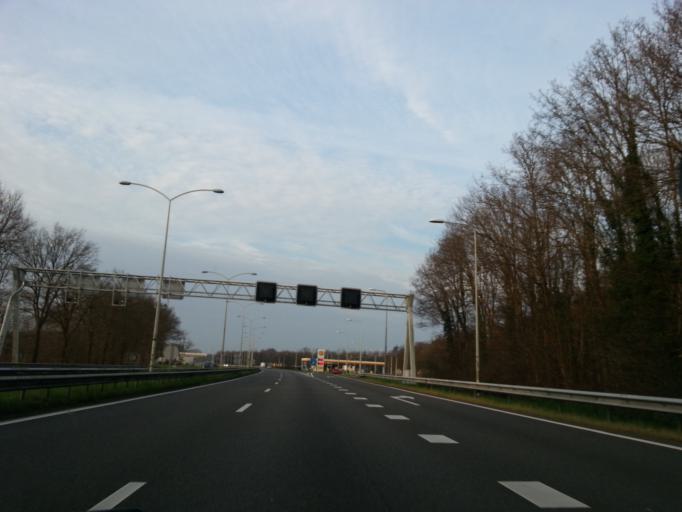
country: NL
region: Gelderland
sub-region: Gemeente Zevenaar
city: Zevenaar
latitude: 51.9039
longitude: 6.1602
